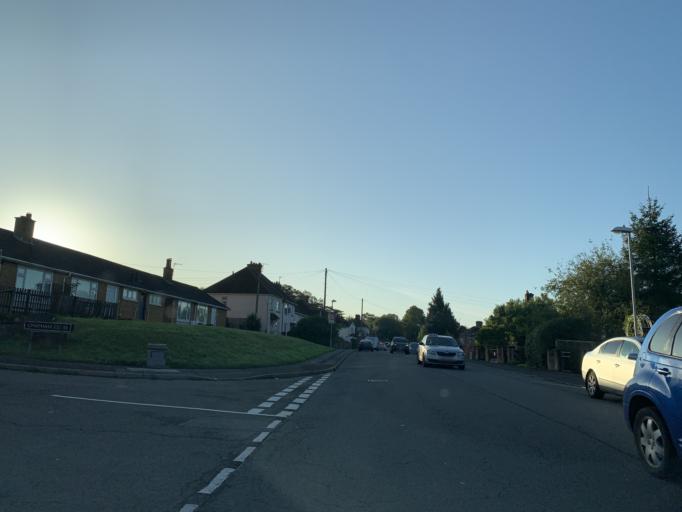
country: GB
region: England
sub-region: Wiltshire
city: Salisbury
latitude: 51.0839
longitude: -1.8035
